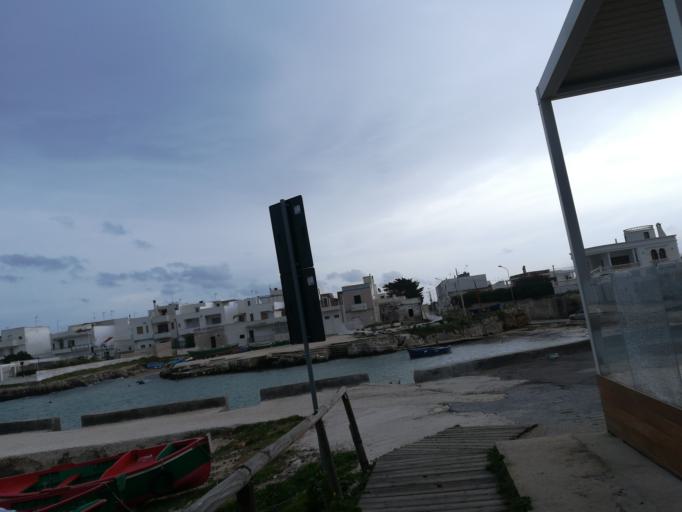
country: IT
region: Apulia
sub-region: Provincia di Bari
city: Polignano a Mare
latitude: 41.0140
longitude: 17.1928
